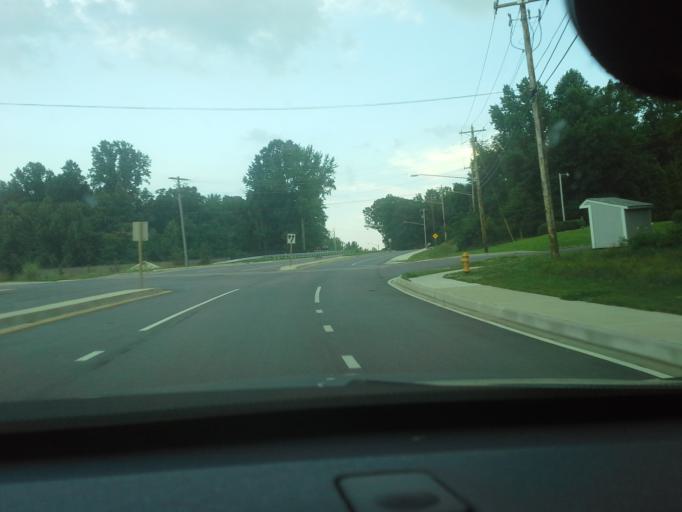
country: US
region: Maryland
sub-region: Calvert County
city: Prince Frederick
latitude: 38.5469
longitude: -76.5846
